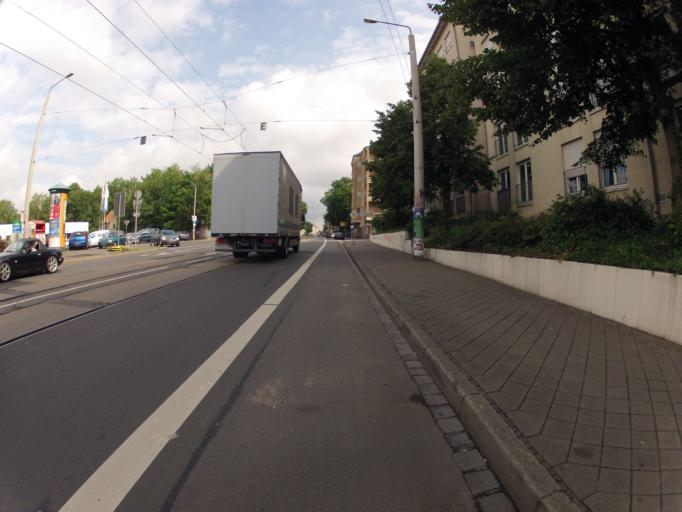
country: DE
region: Saxony
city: Markkleeberg
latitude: 51.3036
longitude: 12.3742
